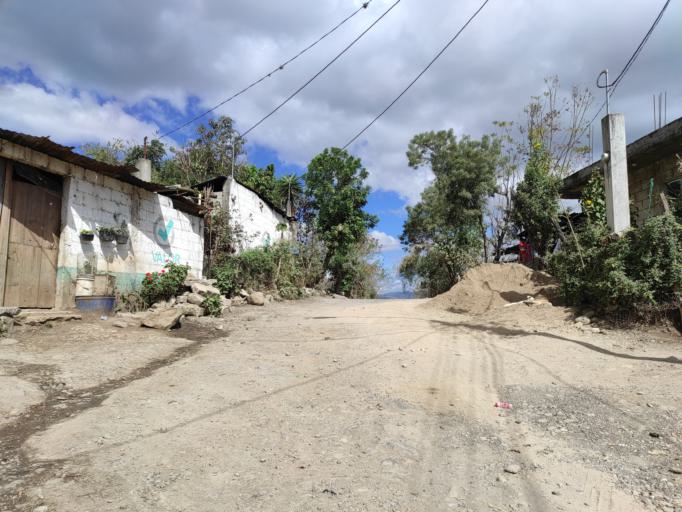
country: GT
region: Guatemala
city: Villa Canales
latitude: 14.4409
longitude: -90.5709
